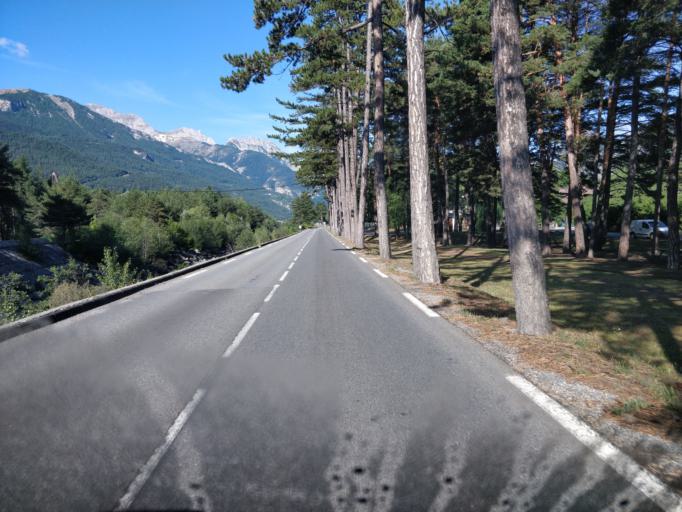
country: FR
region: Provence-Alpes-Cote d'Azur
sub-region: Departement des Alpes-de-Haute-Provence
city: Barcelonnette
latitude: 44.3863
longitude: 6.6328
